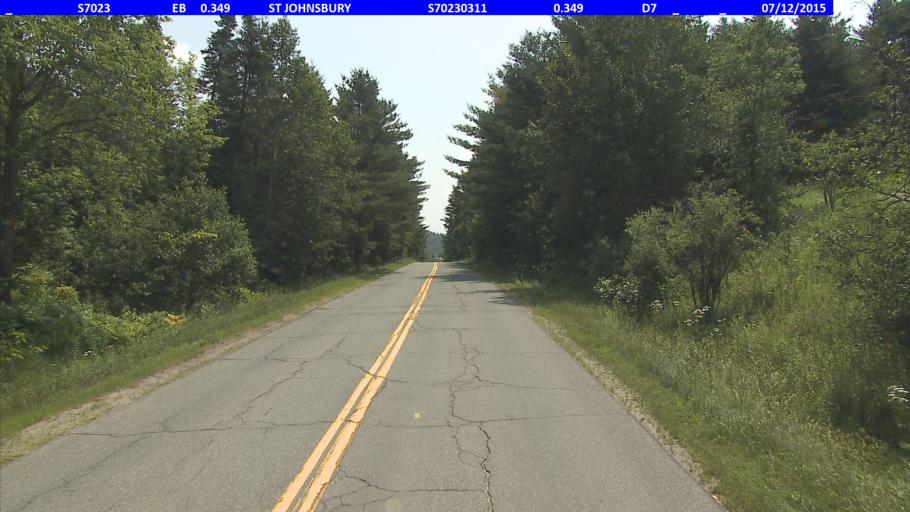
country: US
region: Vermont
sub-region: Caledonia County
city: St Johnsbury
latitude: 44.4457
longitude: -72.0563
